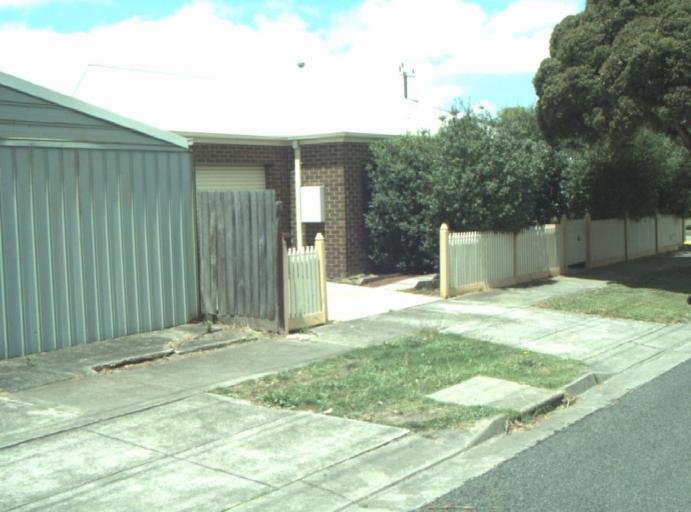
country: AU
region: Victoria
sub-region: Greater Geelong
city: Wandana Heights
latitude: -38.1821
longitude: 144.3279
